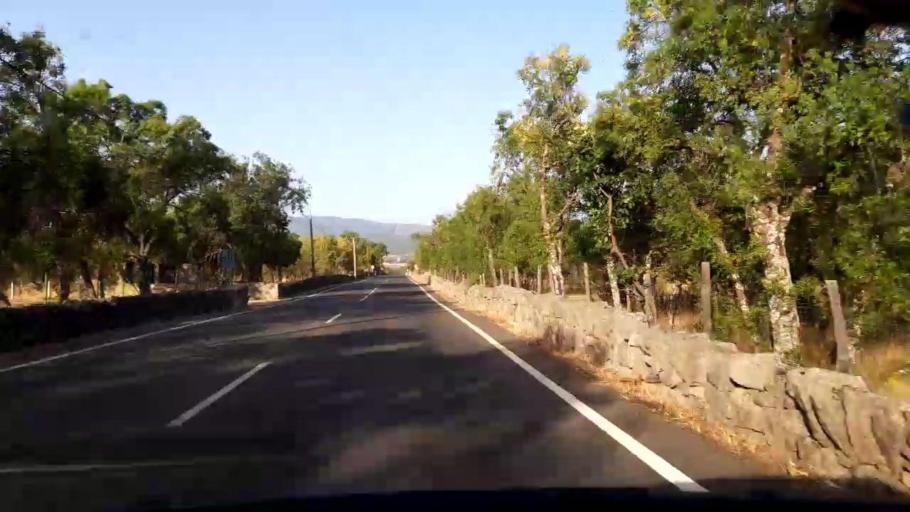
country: ES
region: Madrid
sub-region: Provincia de Madrid
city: Los Molinos
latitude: 40.6875
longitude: -4.0562
